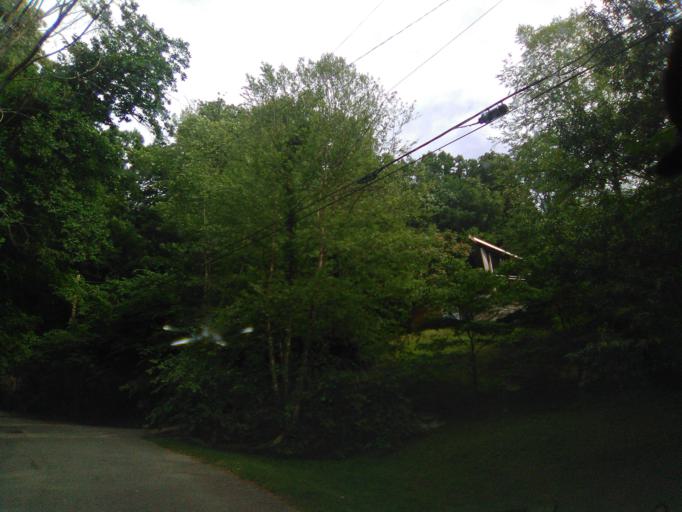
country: US
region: Tennessee
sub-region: Davidson County
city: Belle Meade
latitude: 36.0985
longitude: -86.9120
